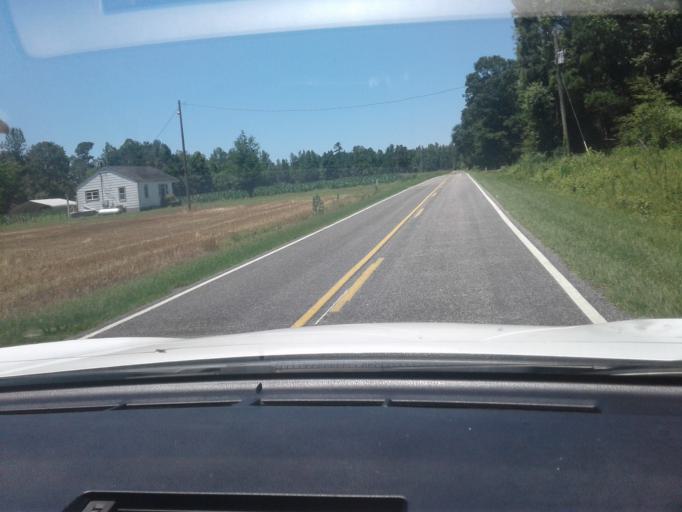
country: US
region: North Carolina
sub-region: Harnett County
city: Lillington
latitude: 35.3429
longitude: -78.9055
